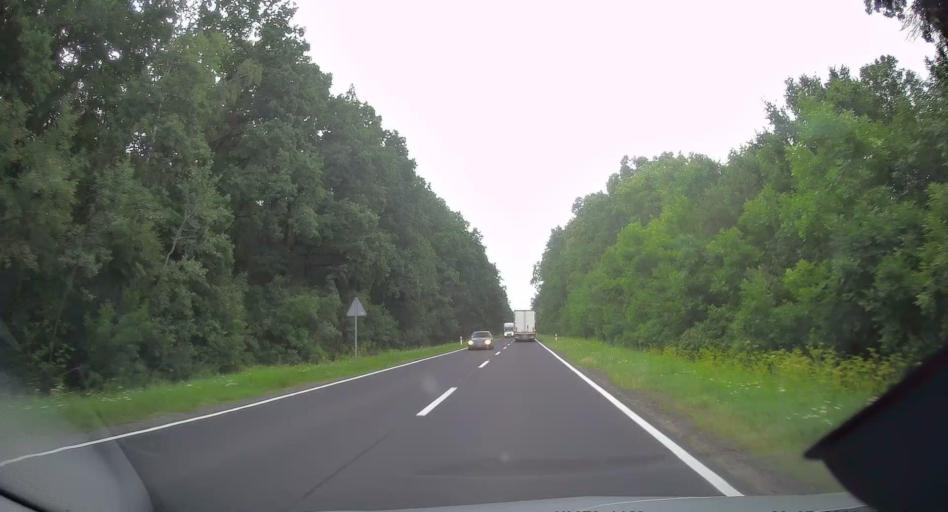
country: PL
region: Silesian Voivodeship
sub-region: Powiat czestochowski
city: Klomnice
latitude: 50.9502
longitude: 19.3979
